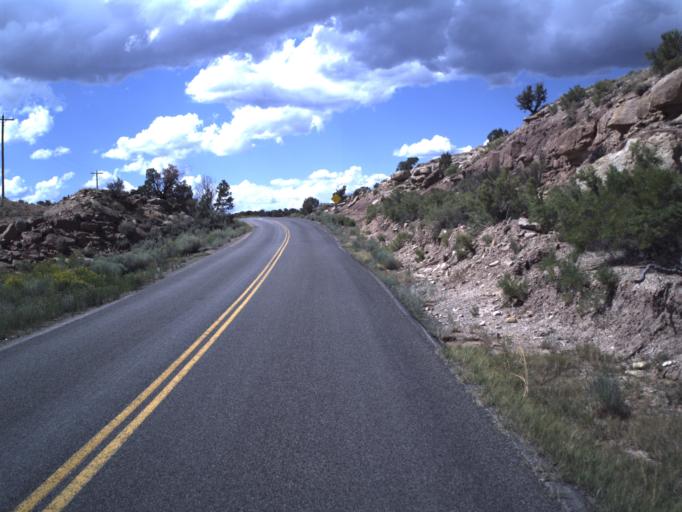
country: US
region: Utah
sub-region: Duchesne County
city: Duchesne
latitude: 40.1751
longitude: -110.4426
